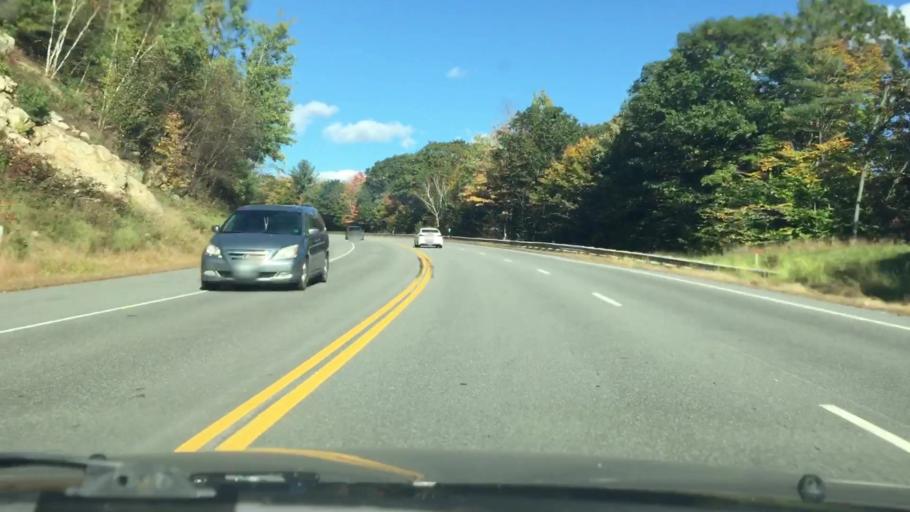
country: US
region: New Hampshire
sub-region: Cheshire County
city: Keene
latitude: 42.9592
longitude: -72.2649
